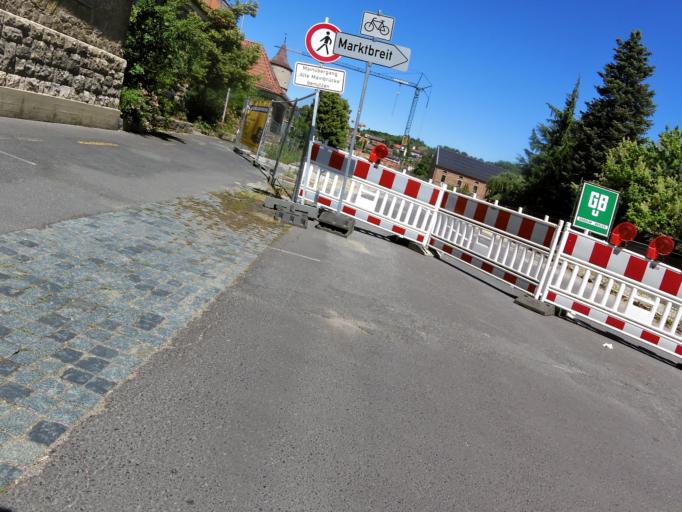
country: DE
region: Bavaria
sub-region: Regierungsbezirk Unterfranken
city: Ochsenfurt
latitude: 49.6646
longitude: 10.0676
